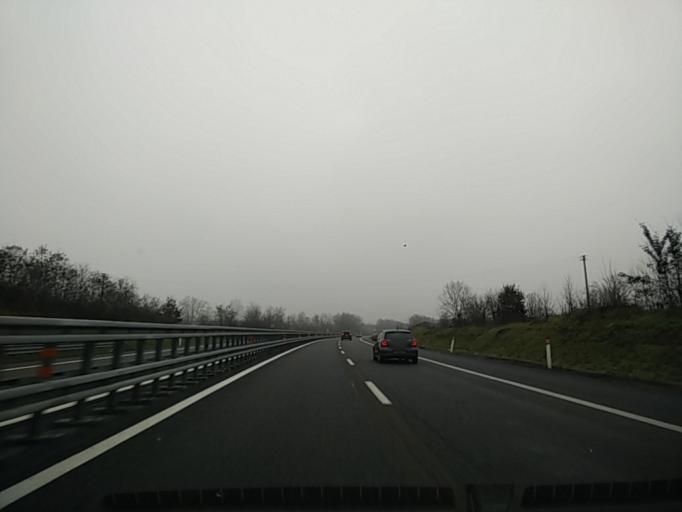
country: IT
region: Piedmont
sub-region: Provincia di Asti
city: Asti
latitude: 44.9138
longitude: 8.1851
